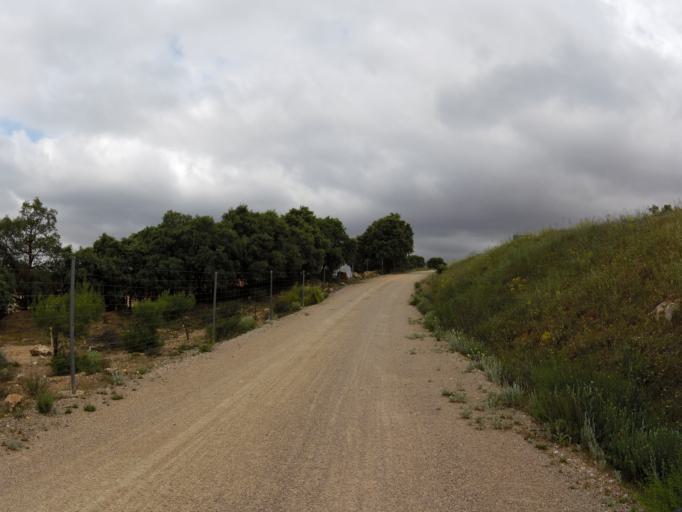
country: ES
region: Castille-La Mancha
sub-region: Provincia de Albacete
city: Robledo
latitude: 38.7339
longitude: -2.4669
